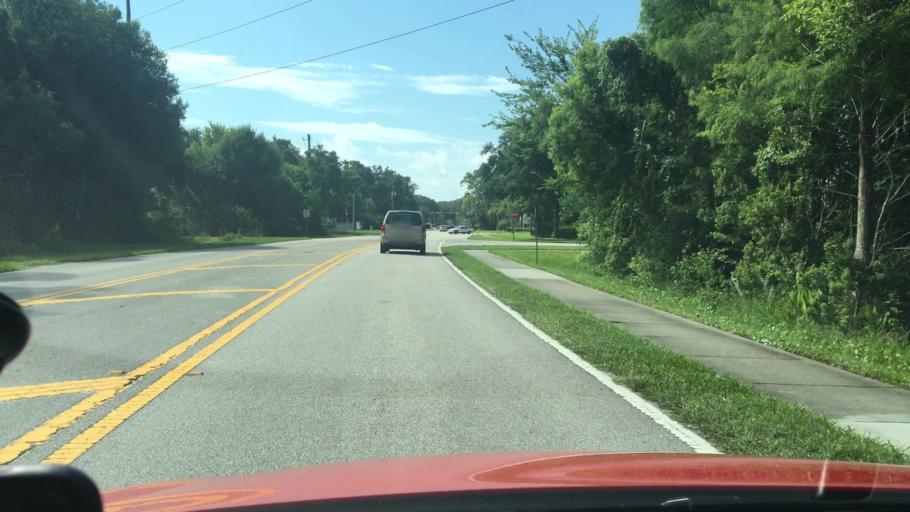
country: US
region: Florida
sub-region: Volusia County
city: New Smyrna Beach
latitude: 29.0175
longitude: -80.9438
